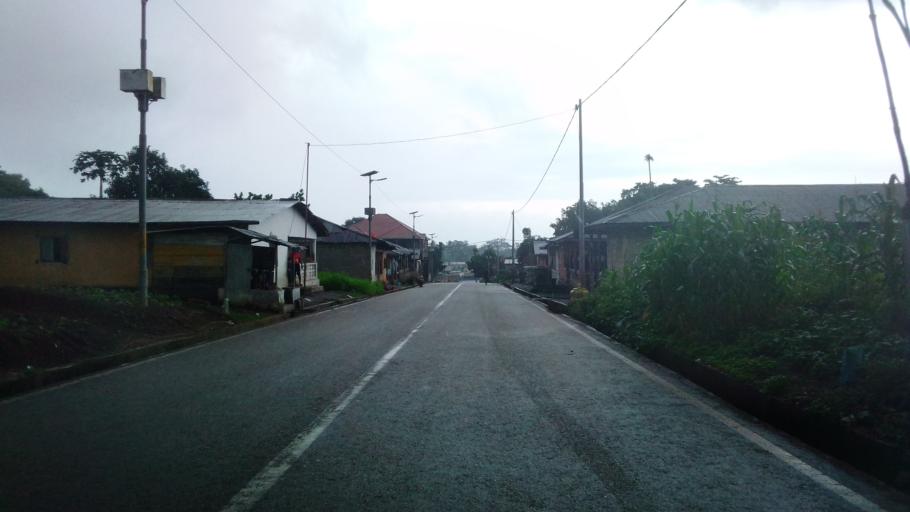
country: SL
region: Northern Province
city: Lunsar
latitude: 8.6836
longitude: -12.5319
